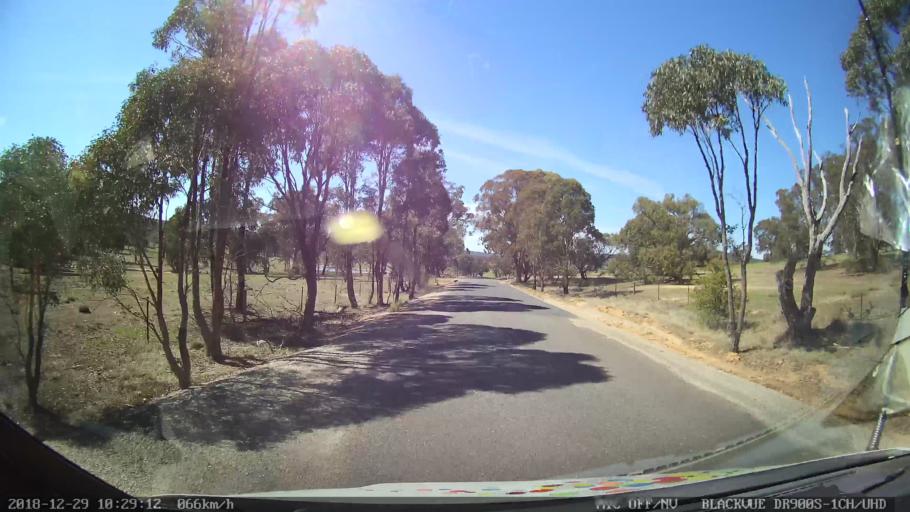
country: AU
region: New South Wales
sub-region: Yass Valley
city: Gundaroo
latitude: -34.9496
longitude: 149.4570
